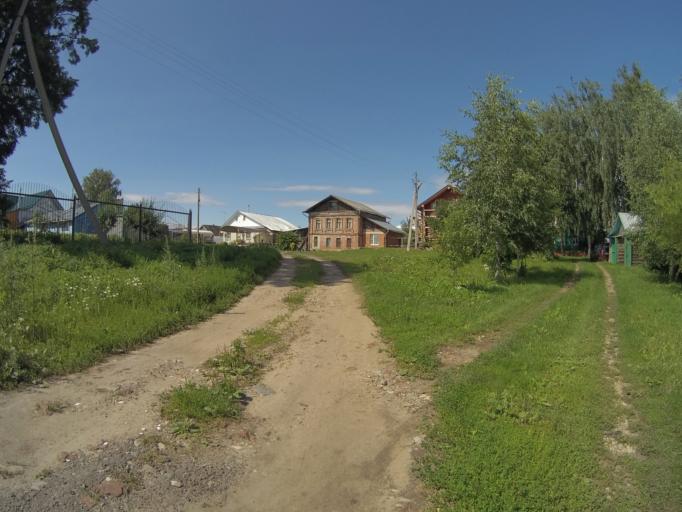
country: RU
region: Vladimir
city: Vladimir
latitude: 56.2674
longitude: 40.3762
